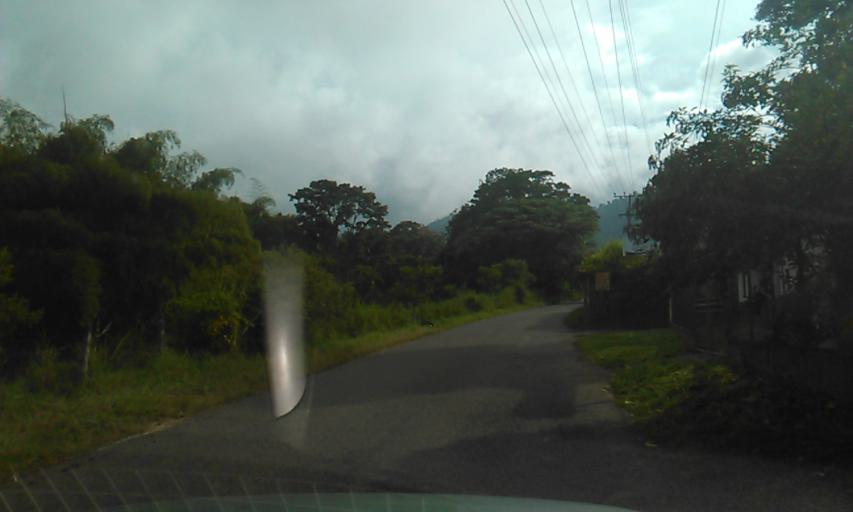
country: CO
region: Quindio
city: Cordoba
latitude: 4.4011
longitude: -75.7187
